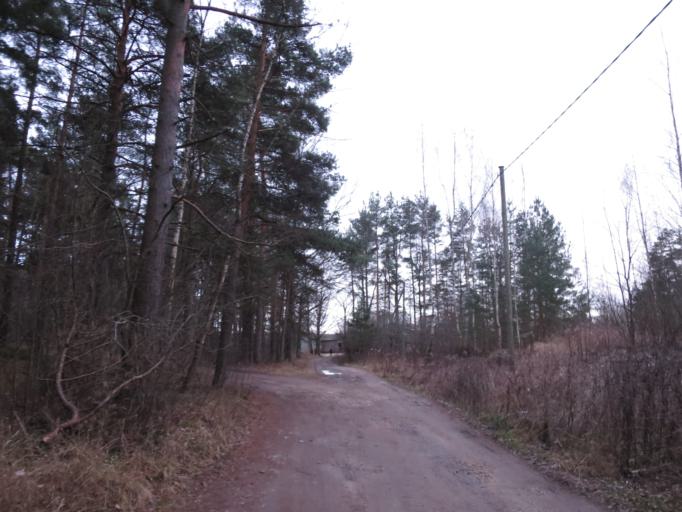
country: LV
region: Riga
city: Bergi
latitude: 56.9765
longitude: 24.3136
